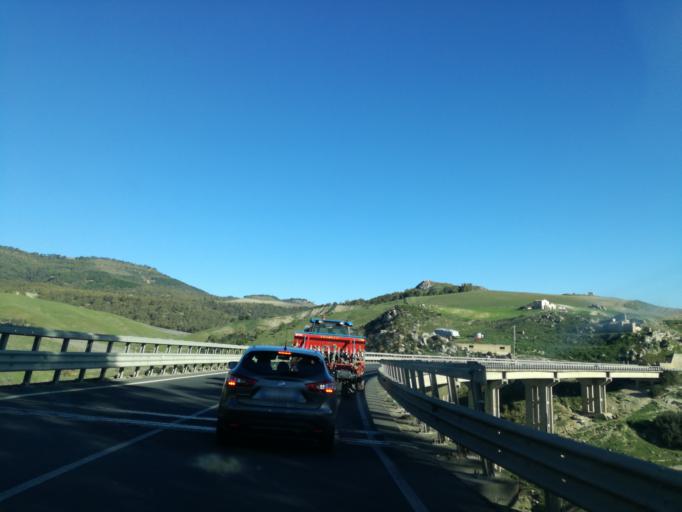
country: IT
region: Sicily
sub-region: Catania
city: San Michele di Ganzaria
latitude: 37.2382
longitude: 14.4501
